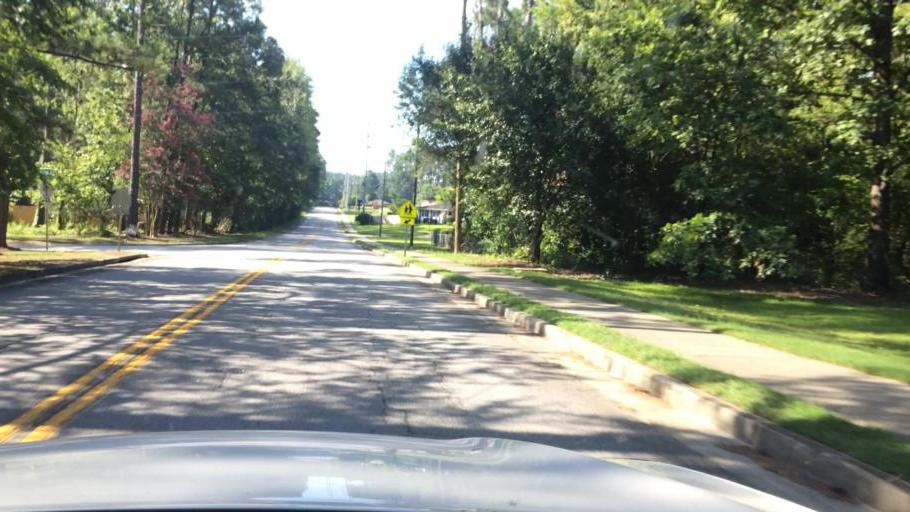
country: US
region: Georgia
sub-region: Columbia County
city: Martinez
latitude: 33.4989
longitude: -82.0398
